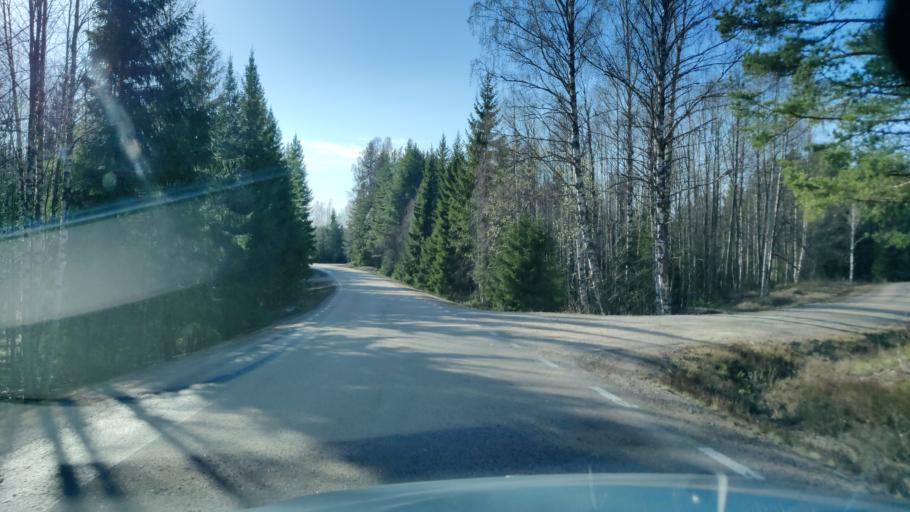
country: SE
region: Vaermland
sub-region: Sunne Kommun
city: Sunne
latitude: 59.9869
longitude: 13.3347
